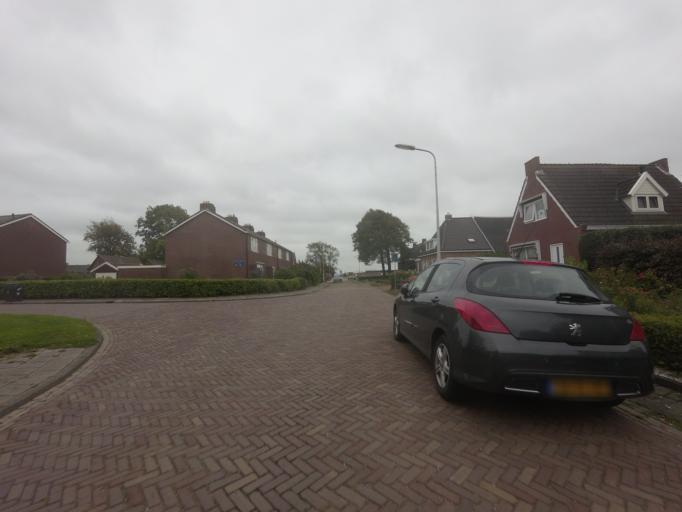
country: NL
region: Friesland
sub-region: Gemeente Ferwerderadiel
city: Ferwert
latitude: 53.3504
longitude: 5.8612
